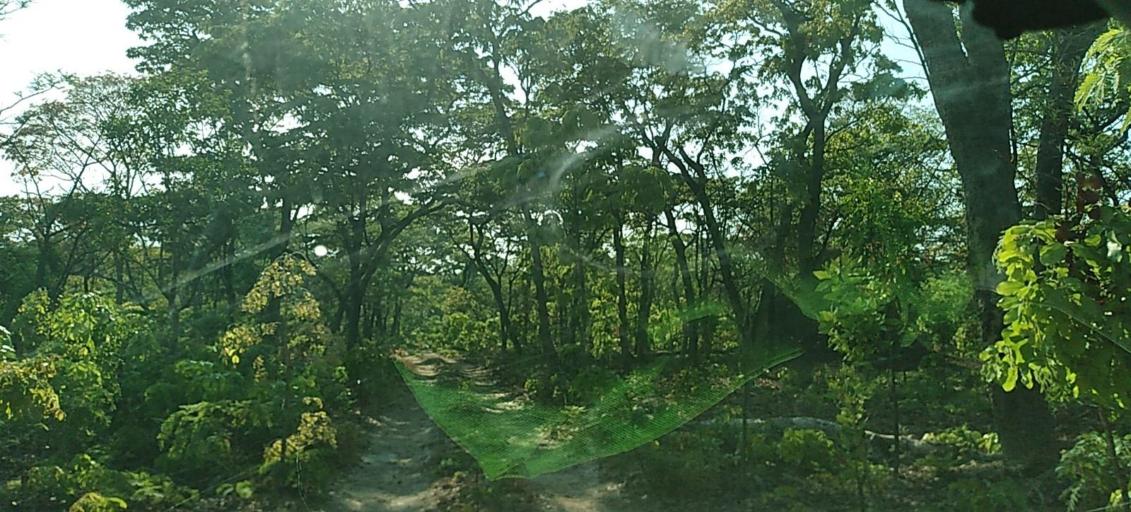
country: ZM
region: North-Western
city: Kalengwa
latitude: -13.2348
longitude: 25.0633
